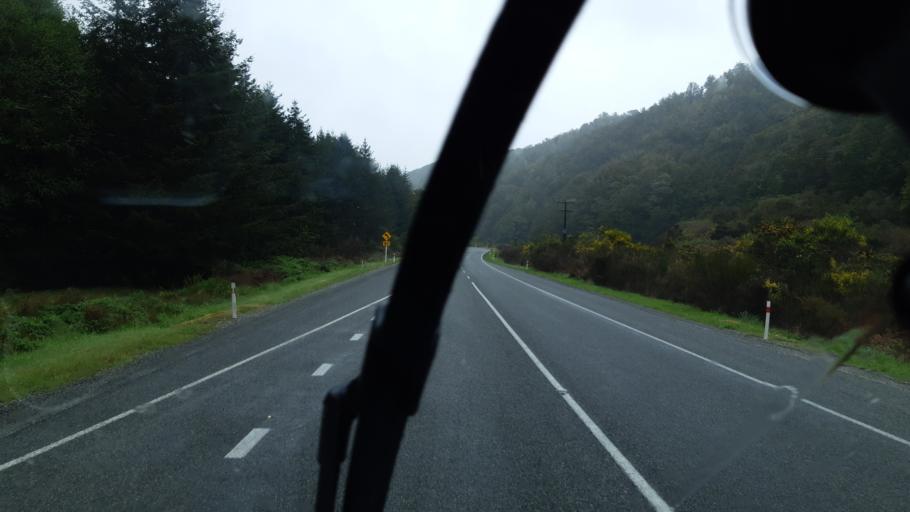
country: NZ
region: West Coast
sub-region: Buller District
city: Westport
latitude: -42.1500
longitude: 171.7869
